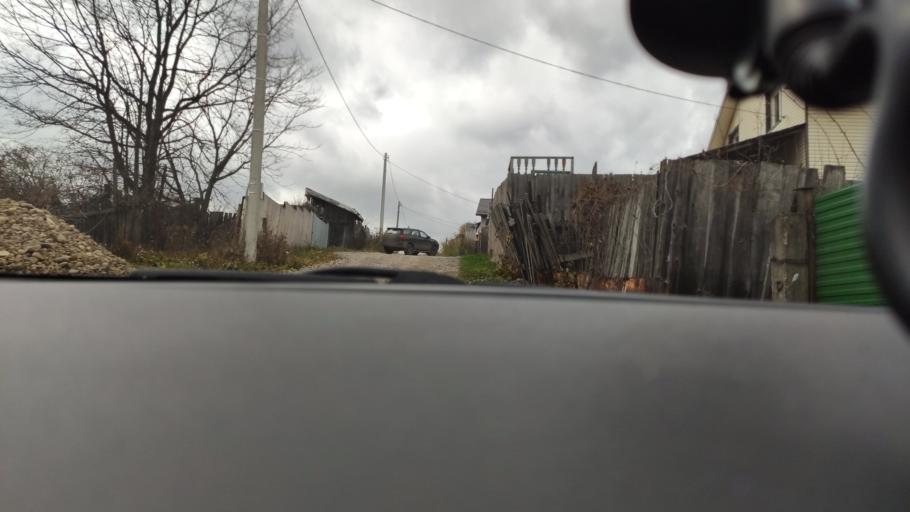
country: RU
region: Perm
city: Perm
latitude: 57.9917
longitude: 56.3127
